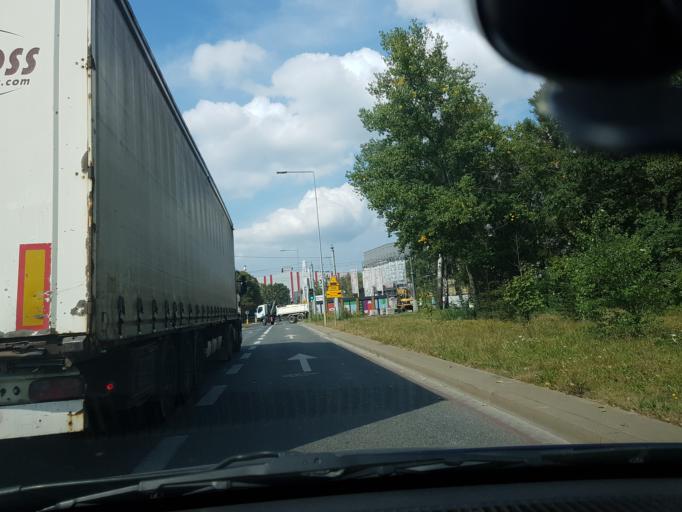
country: PL
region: Masovian Voivodeship
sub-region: Warszawa
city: Bielany
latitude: 52.2925
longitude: 20.9303
